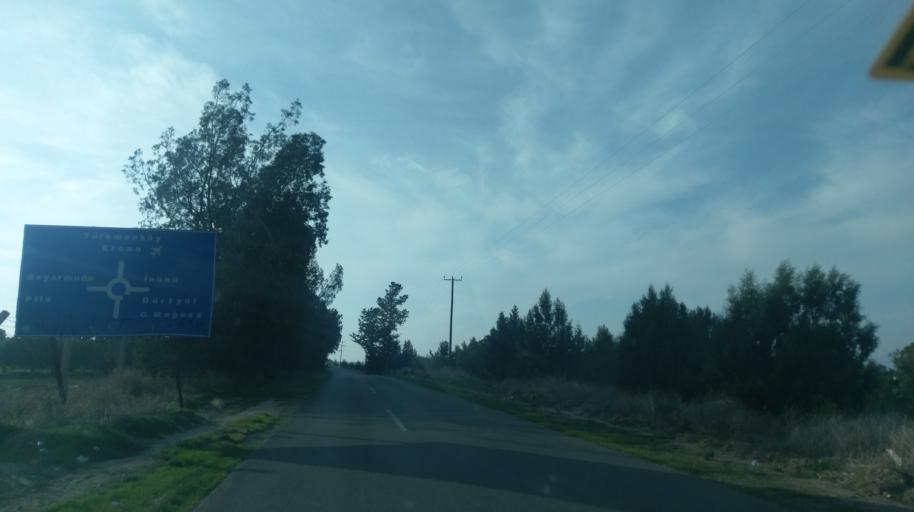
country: CY
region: Larnaka
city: Pergamos
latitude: 35.1106
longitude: 33.7342
